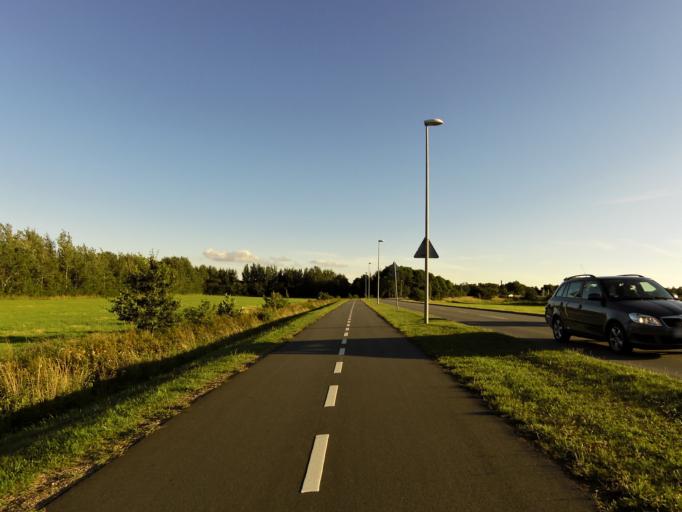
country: DK
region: South Denmark
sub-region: Esbjerg Kommune
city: Ribe
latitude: 55.3361
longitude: 8.7760
